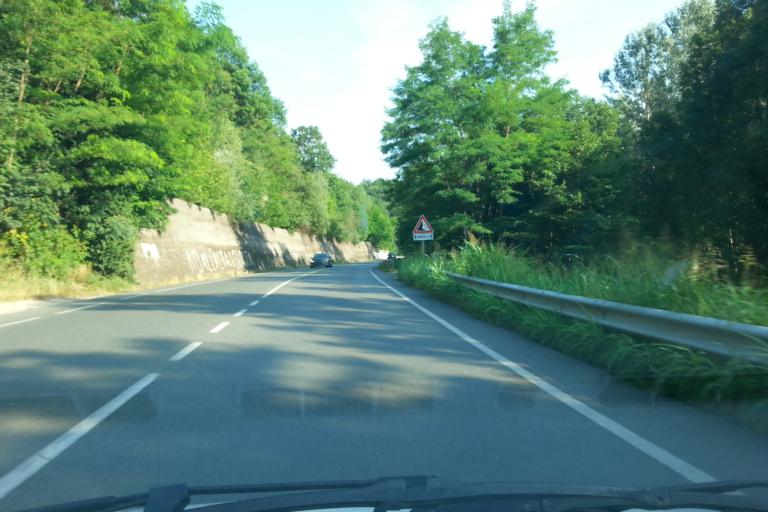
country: IT
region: Piedmont
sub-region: Provincia di Torino
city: Sant'Ambrogio di Torino
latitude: 45.1091
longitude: 7.3700
